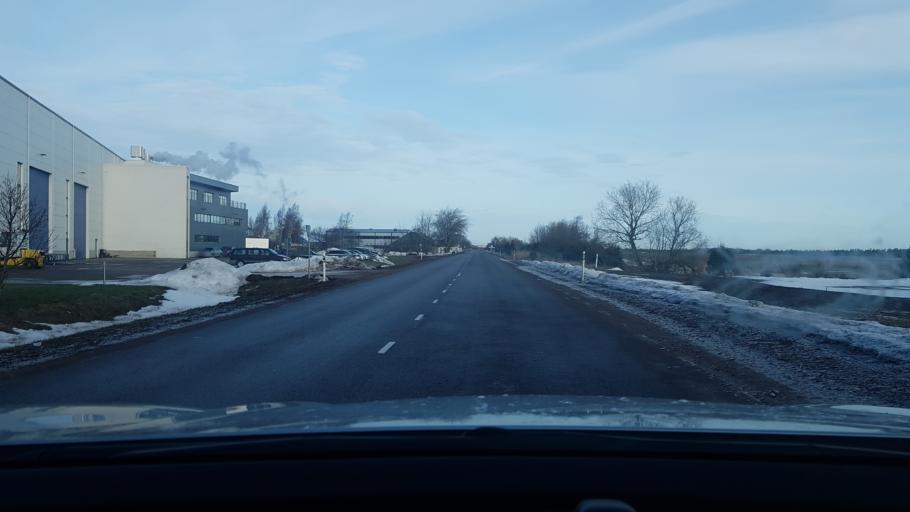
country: EE
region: Saare
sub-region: Kuressaare linn
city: Kuressaare
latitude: 58.2204
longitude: 22.5071
